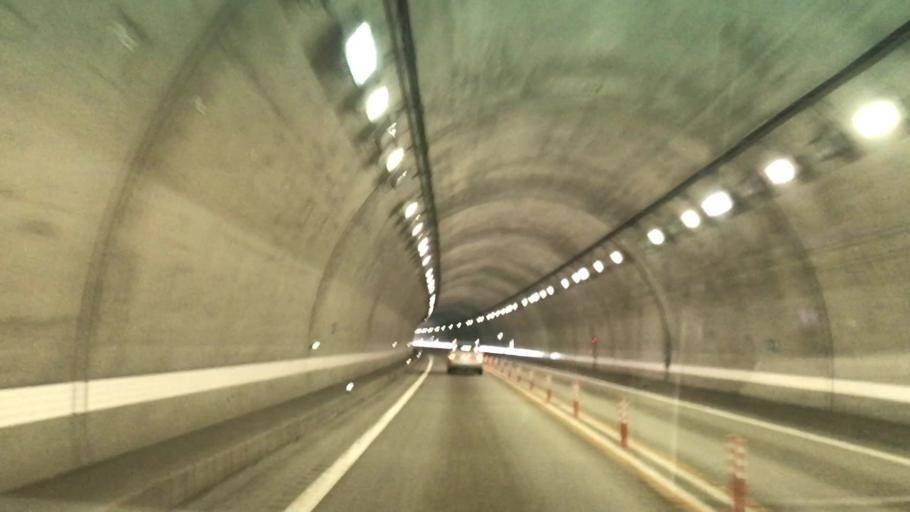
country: JP
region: Hokkaido
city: Iwamizawa
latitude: 42.9311
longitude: 142.0611
